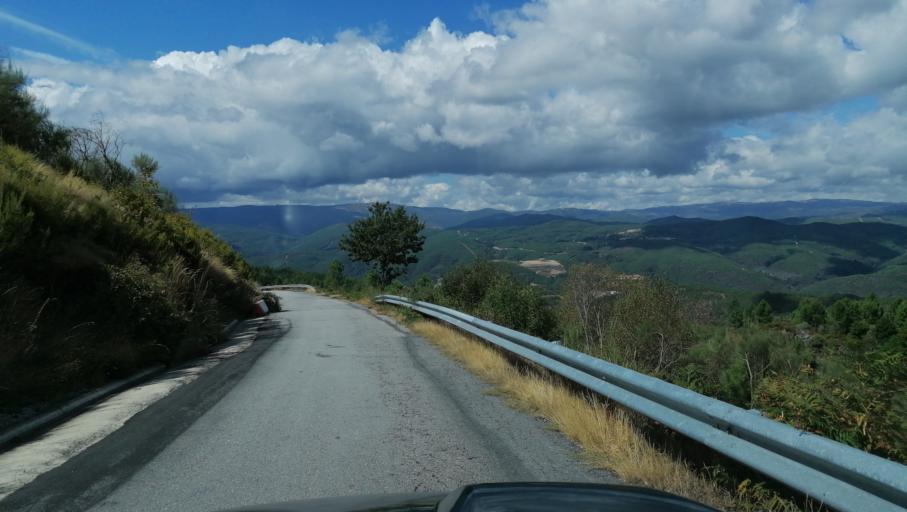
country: PT
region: Vila Real
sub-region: Vila Pouca de Aguiar
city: Vila Pouca de Aguiar
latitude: 41.5561
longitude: -7.7019
